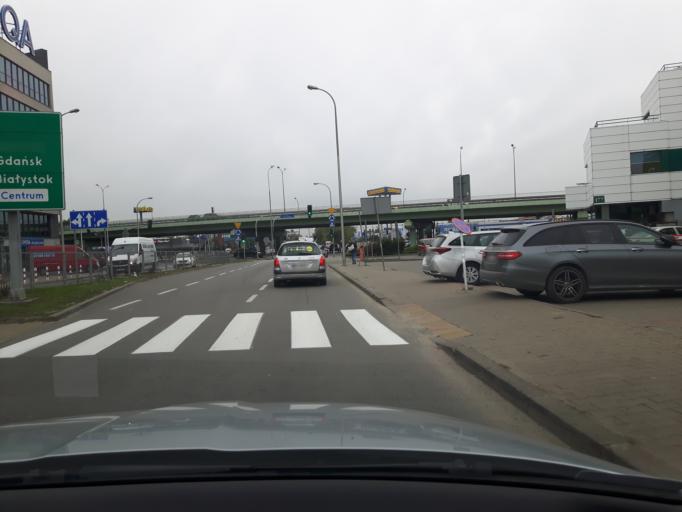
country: PL
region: Masovian Voivodeship
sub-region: Warszawa
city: Wlochy
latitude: 52.2010
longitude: 20.9377
